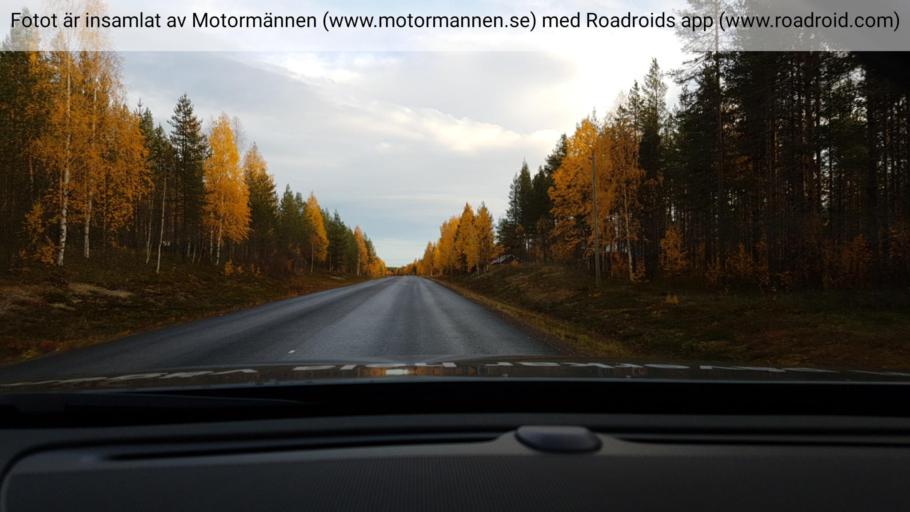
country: SE
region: Norrbotten
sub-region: Overkalix Kommun
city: OEverkalix
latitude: 67.0083
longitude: 22.5391
